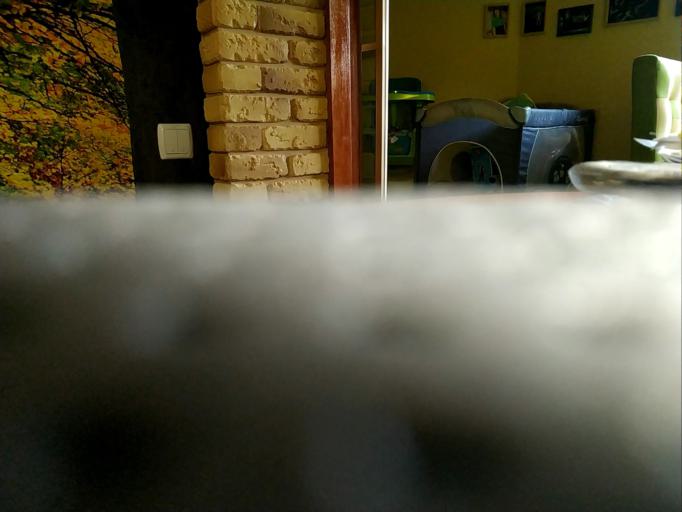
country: RU
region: Kaluga
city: Seredeyskiy
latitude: 53.8672
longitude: 35.3679
